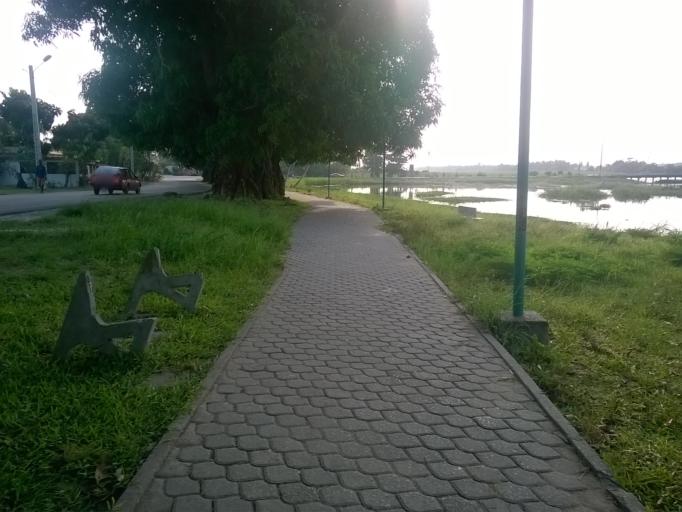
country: CI
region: Sud-Comoe
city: Grand-Bassam
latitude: 5.1976
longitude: -3.7357
